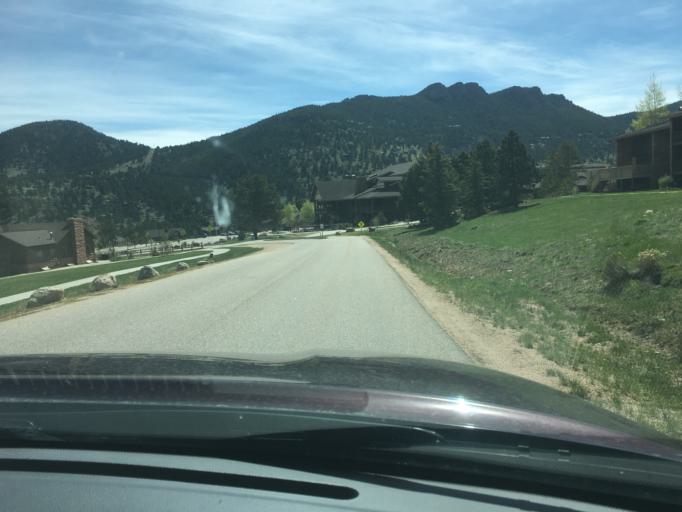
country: US
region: Colorado
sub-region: Larimer County
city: Estes Park
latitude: 40.3402
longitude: -105.5755
